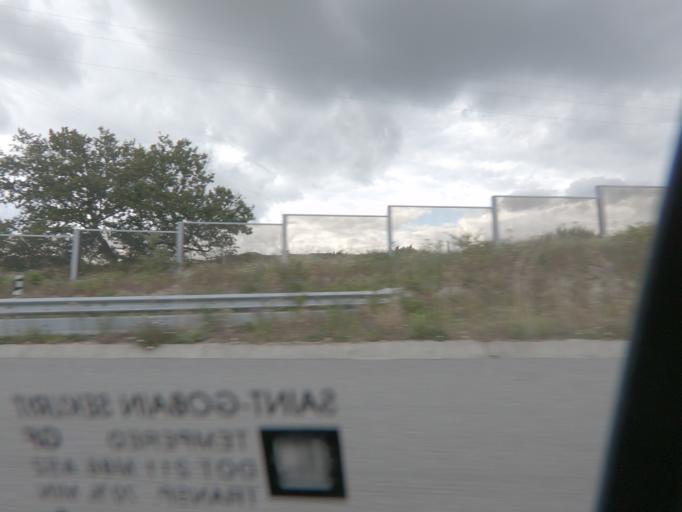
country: PT
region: Porto
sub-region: Amarante
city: Amarante
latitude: 41.2626
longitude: -8.0124
